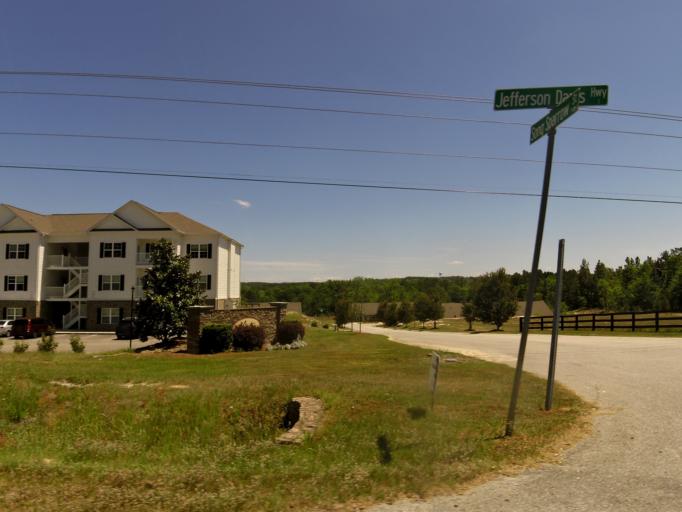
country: US
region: South Carolina
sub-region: Aiken County
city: Burnettown
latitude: 33.5195
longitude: -81.8569
